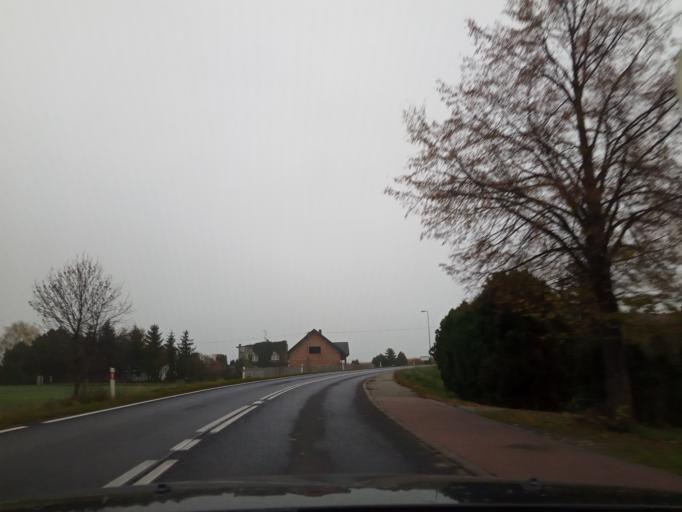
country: PL
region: Lesser Poland Voivodeship
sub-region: Powiat proszowicki
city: Proszowice
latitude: 50.1602
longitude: 20.1910
